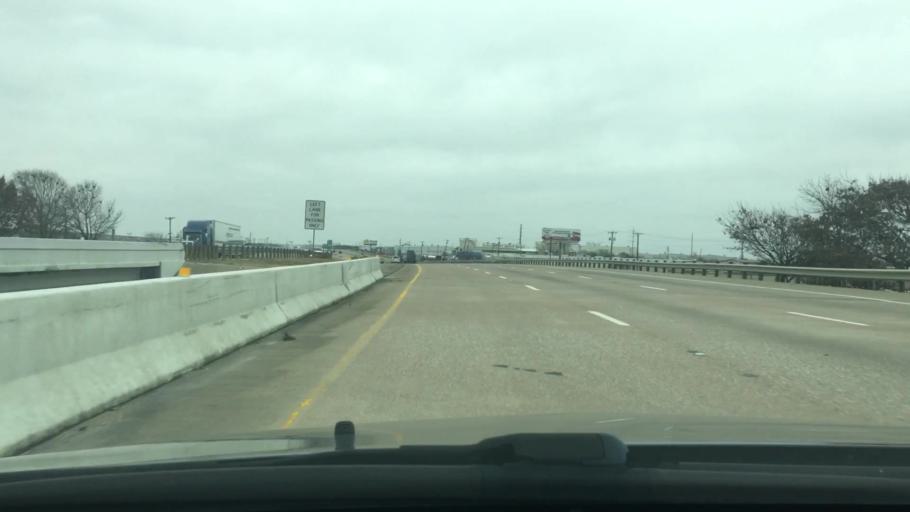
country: US
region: Texas
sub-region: Ellis County
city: Ennis
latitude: 32.3105
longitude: -96.5967
